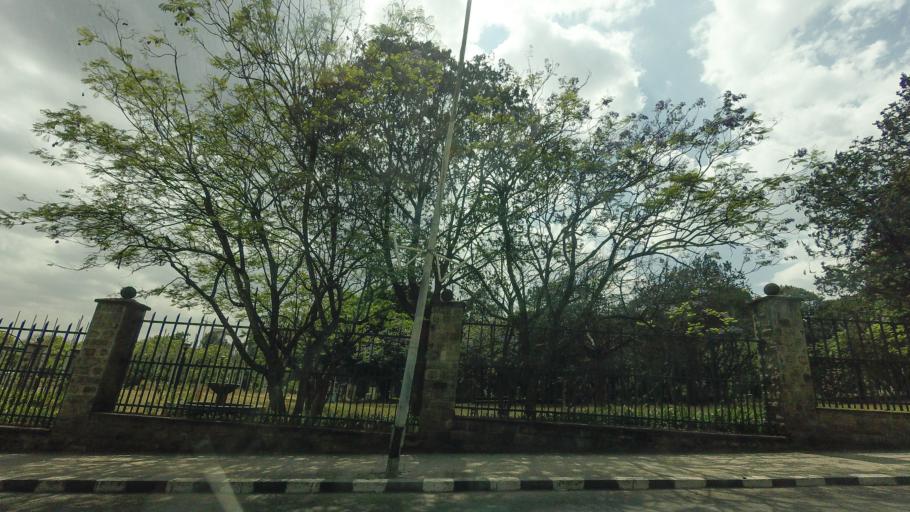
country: ET
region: Adis Abeba
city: Addis Ababa
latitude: 9.0155
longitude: 38.7636
